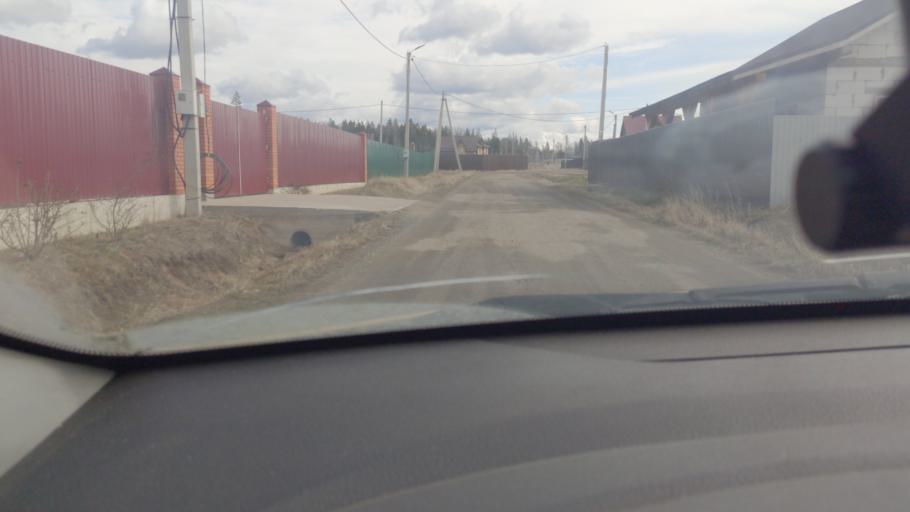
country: RU
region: Moskovskaya
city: Ruza
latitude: 55.7631
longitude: 36.1365
